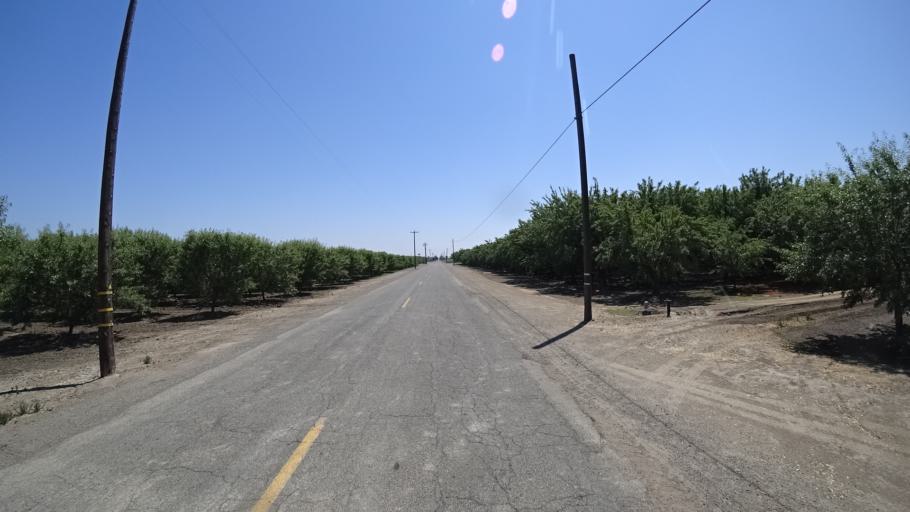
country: US
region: California
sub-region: Kings County
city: Armona
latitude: 36.3572
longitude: -119.7384
